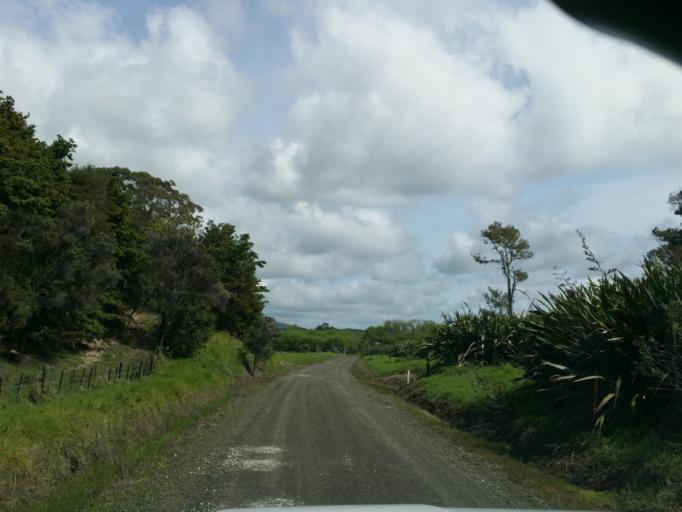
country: NZ
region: Northland
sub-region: Whangarei
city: Maungatapere
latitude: -35.8316
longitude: 174.0526
